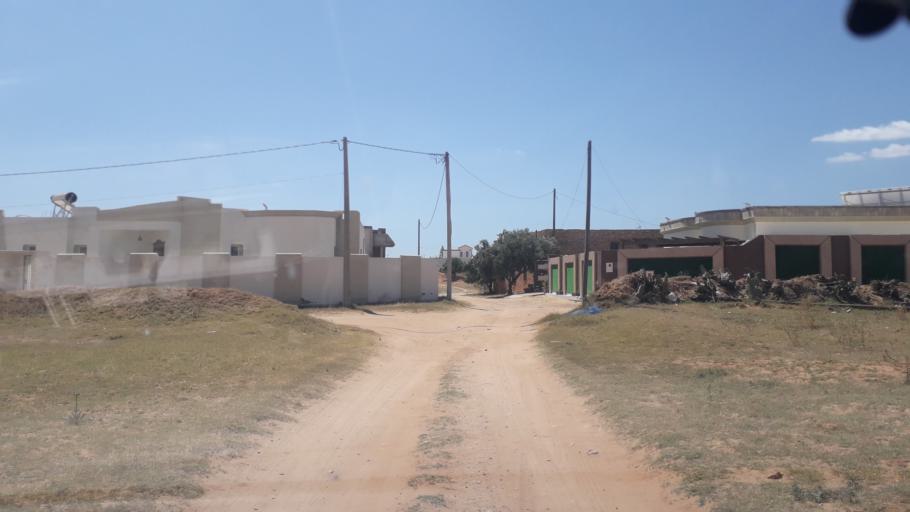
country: TN
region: Safaqis
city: Al Qarmadah
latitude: 34.8315
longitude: 10.7703
